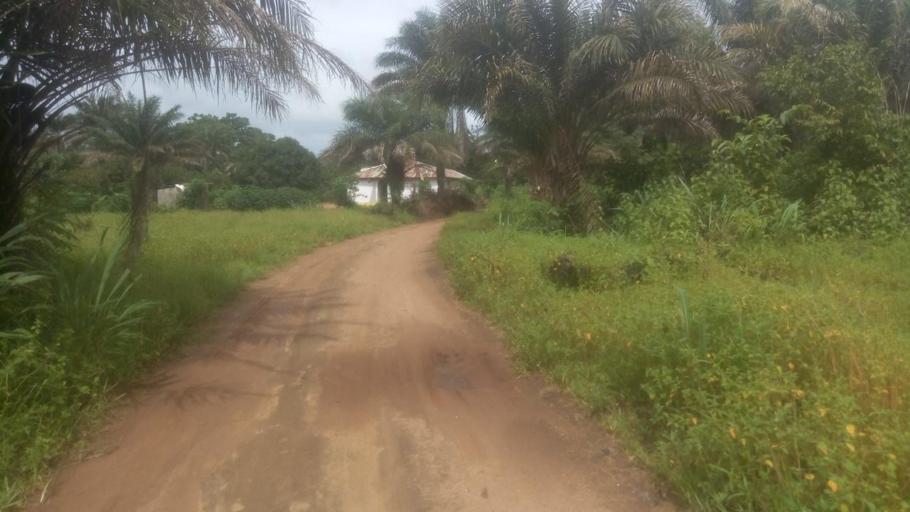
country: SL
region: Northern Province
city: Masoyila
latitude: 8.5910
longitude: -13.1887
